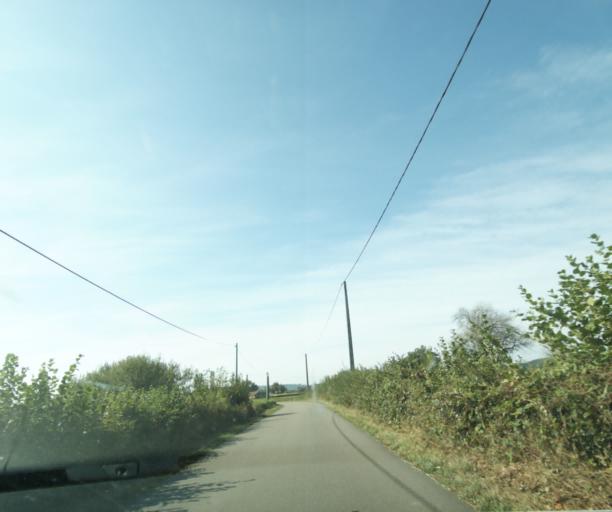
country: FR
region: Bourgogne
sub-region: Departement de Saone-et-Loire
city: Ciry-le-Noble
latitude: 46.5598
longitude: 4.3315
